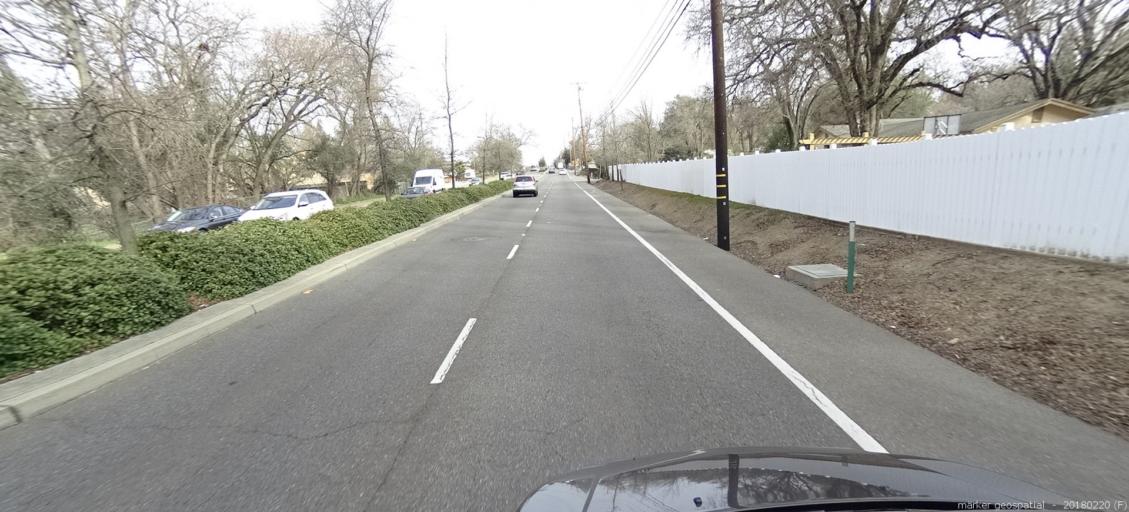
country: US
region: California
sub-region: Sacramento County
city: Orangevale
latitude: 38.7033
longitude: -121.2251
